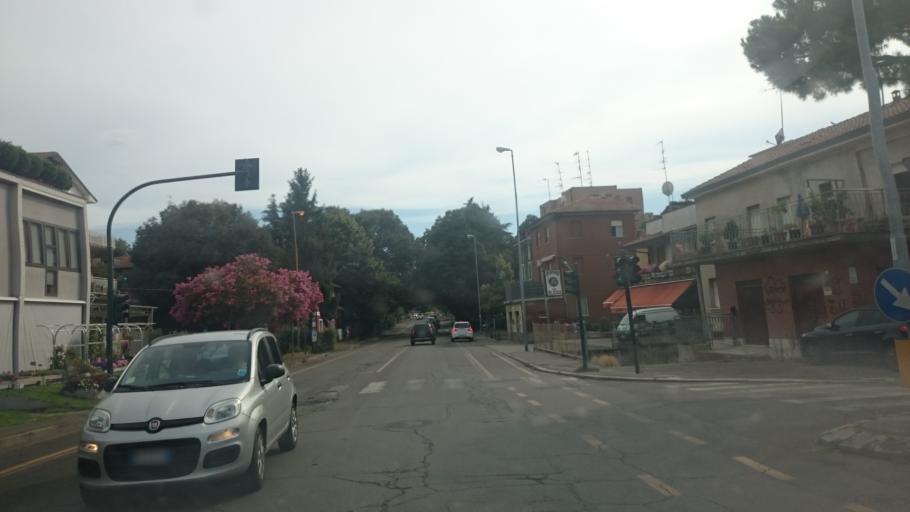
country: IT
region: Emilia-Romagna
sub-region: Provincia di Reggio Emilia
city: Reggio nell'Emilia
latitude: 44.6834
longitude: 10.6224
